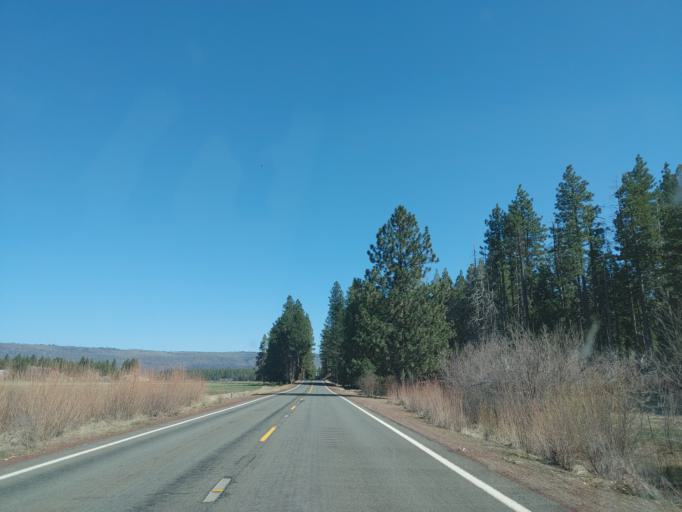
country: US
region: California
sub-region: Shasta County
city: Burney
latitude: 40.7449
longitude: -121.4785
